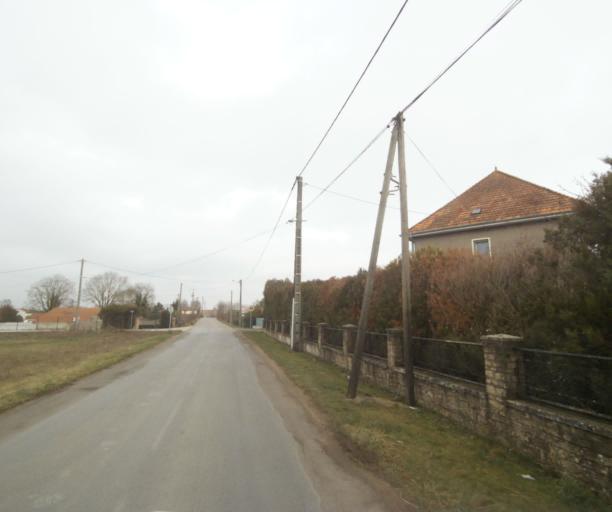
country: FR
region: Champagne-Ardenne
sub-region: Departement de la Haute-Marne
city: Villiers-en-Lieu
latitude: 48.6514
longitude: 4.8203
